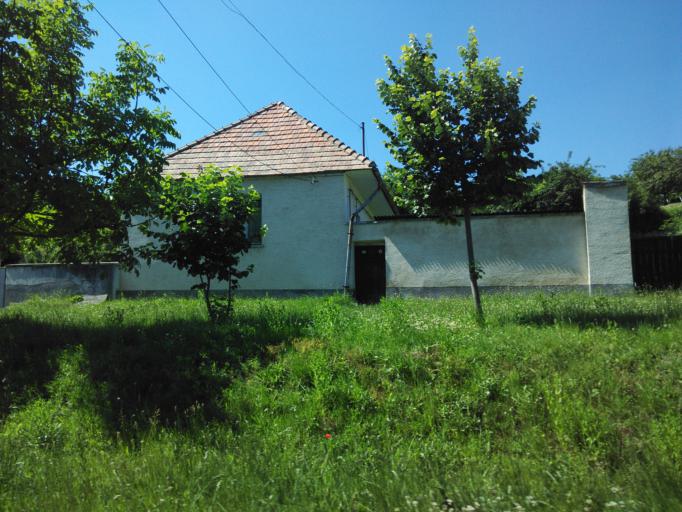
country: HU
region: Fejer
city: Mor
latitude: 47.3756
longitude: 18.2220
